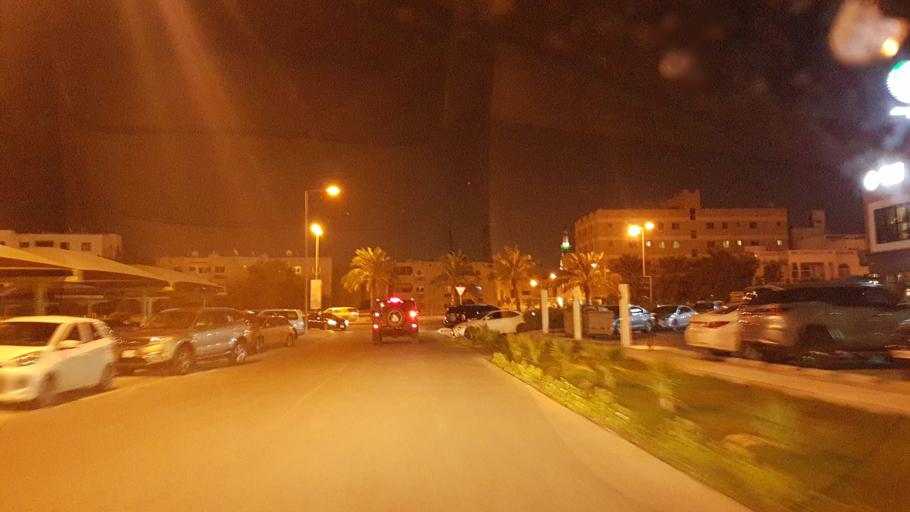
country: BH
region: Manama
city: Jidd Hafs
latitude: 26.2299
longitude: 50.5500
